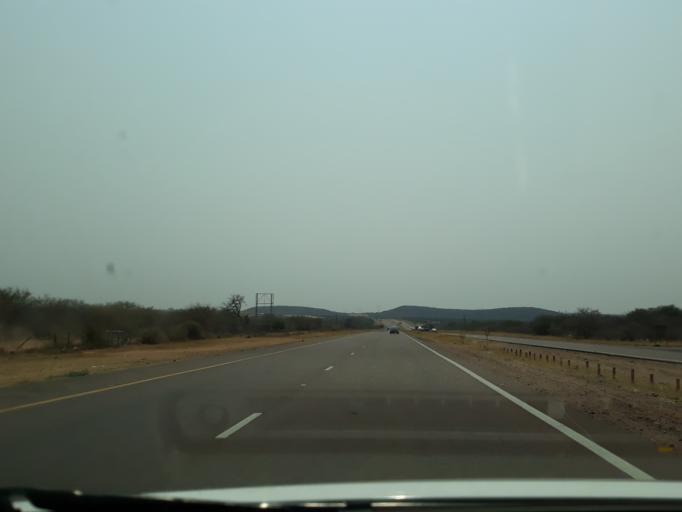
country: BW
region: Kgatleng
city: Bokaa
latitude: -24.4110
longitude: 26.0514
